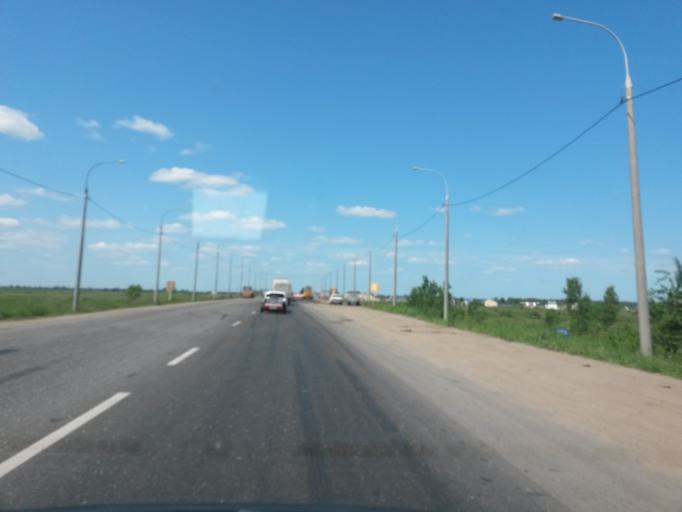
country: RU
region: Jaroslavl
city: Yaroslavl
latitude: 57.6280
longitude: 39.7594
